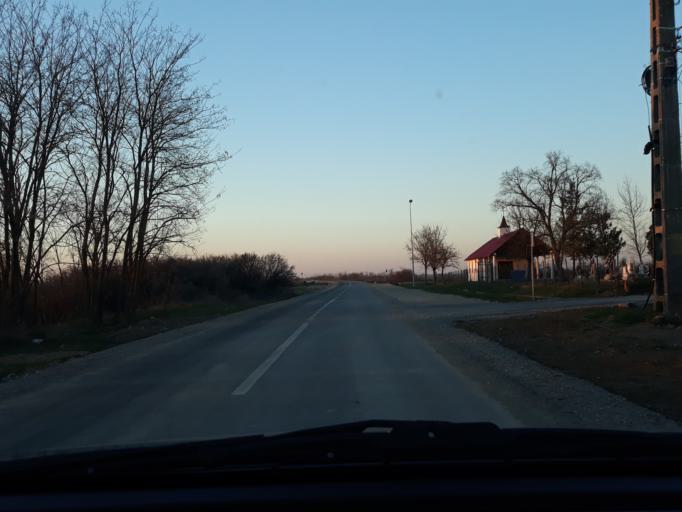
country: RO
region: Bihor
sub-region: Comuna Gepiu
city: Gepiu
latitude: 46.9106
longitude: 21.7878
